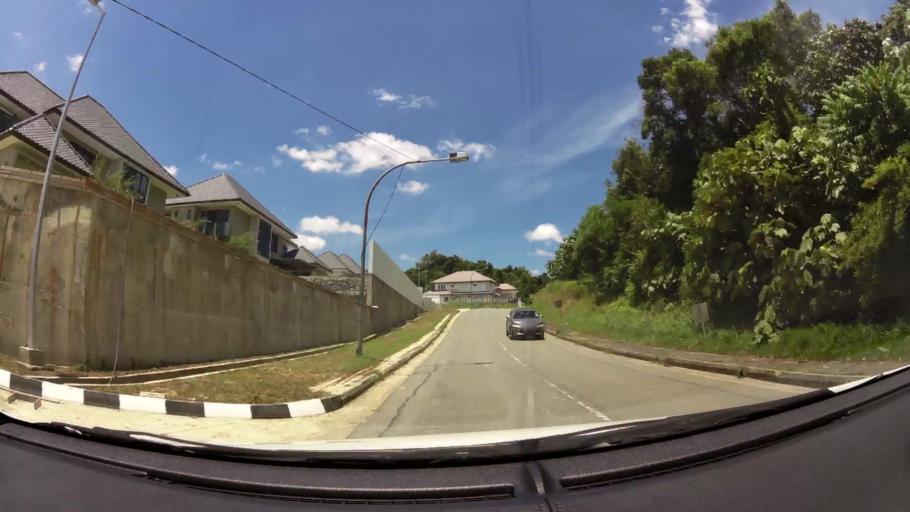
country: BN
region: Brunei and Muara
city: Bandar Seri Begawan
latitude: 4.9414
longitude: 114.9627
